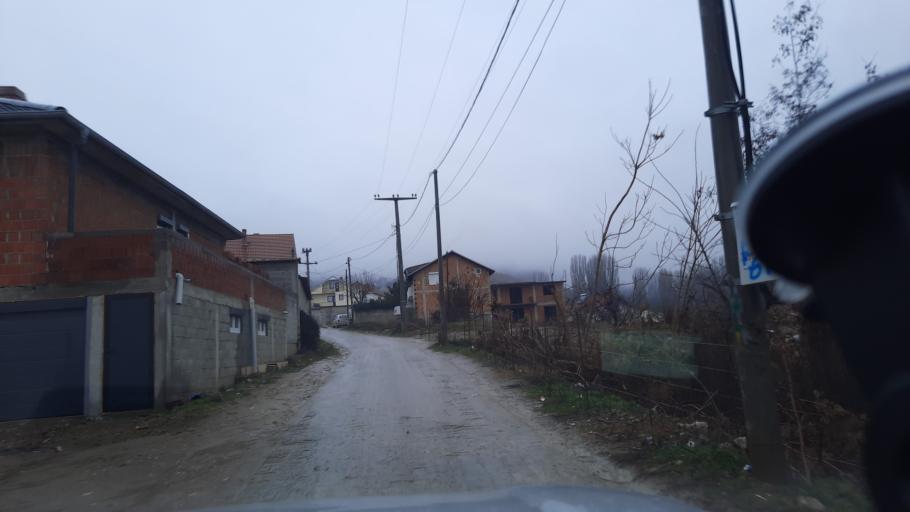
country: MK
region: Opstina Lipkovo
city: Matejche
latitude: 42.1245
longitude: 21.5942
